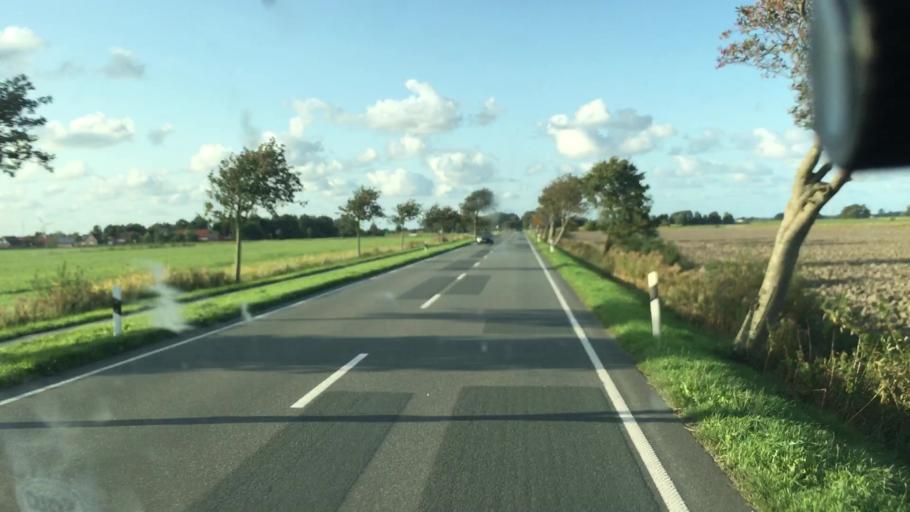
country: DE
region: Lower Saxony
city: Werdum
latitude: 53.6479
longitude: 7.7900
